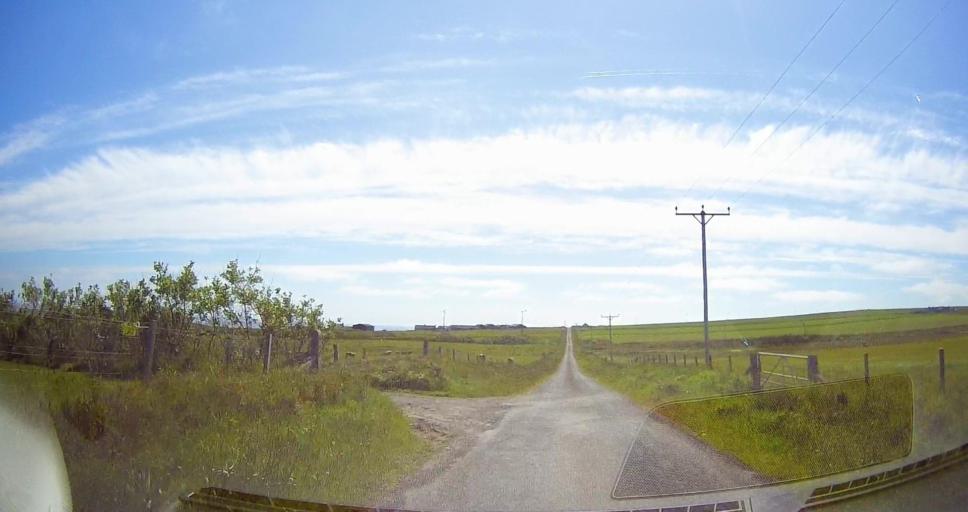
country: GB
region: Scotland
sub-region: Orkney Islands
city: Kirkwall
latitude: 58.8255
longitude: -2.9103
